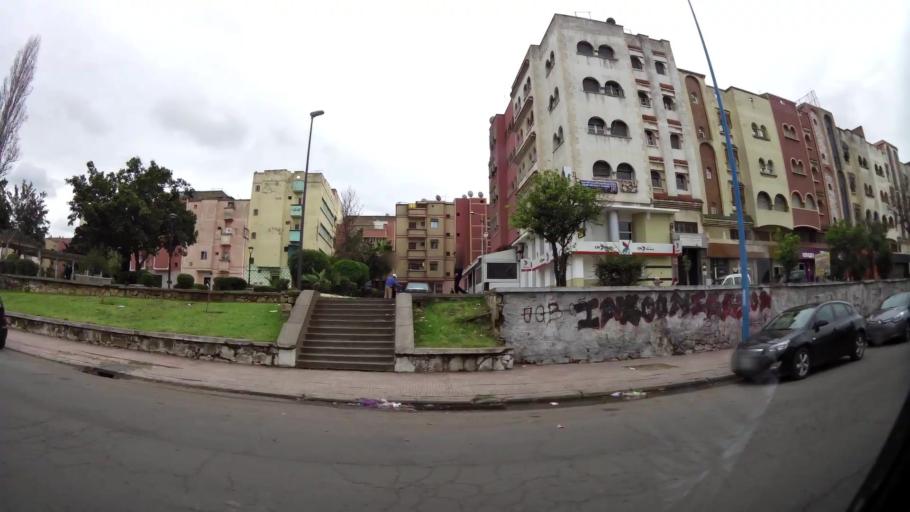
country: MA
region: Grand Casablanca
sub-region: Casablanca
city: Casablanca
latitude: 33.5707
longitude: -7.5561
